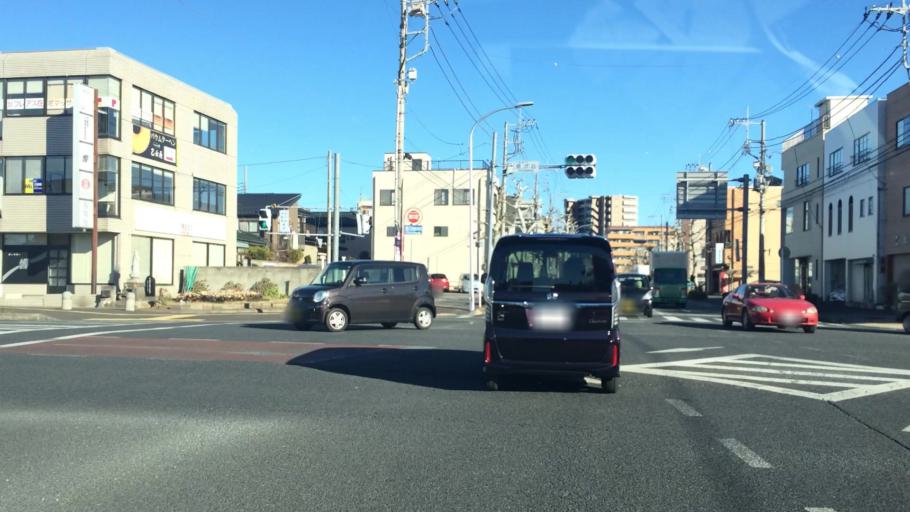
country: JP
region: Tochigi
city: Utsunomiya-shi
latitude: 36.5628
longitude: 139.9156
